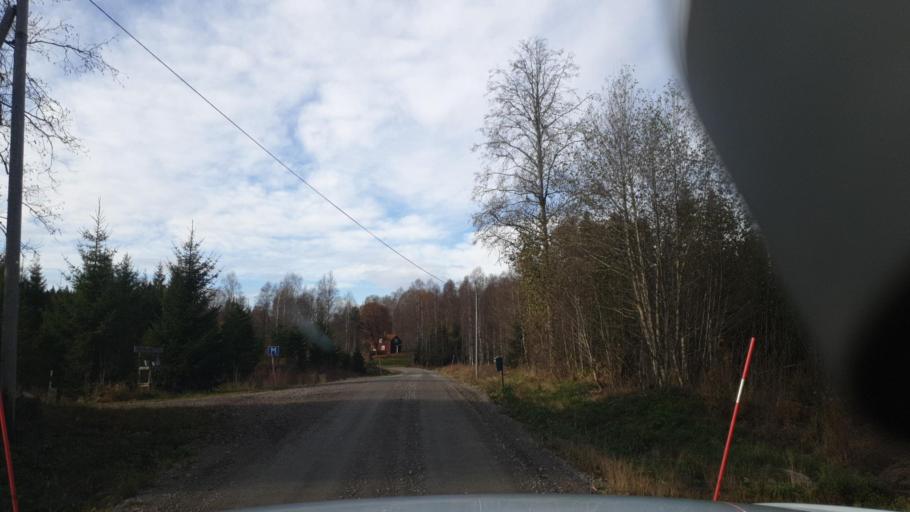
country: SE
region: Vaermland
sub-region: Eda Kommun
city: Charlottenberg
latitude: 59.9904
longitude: 12.4756
